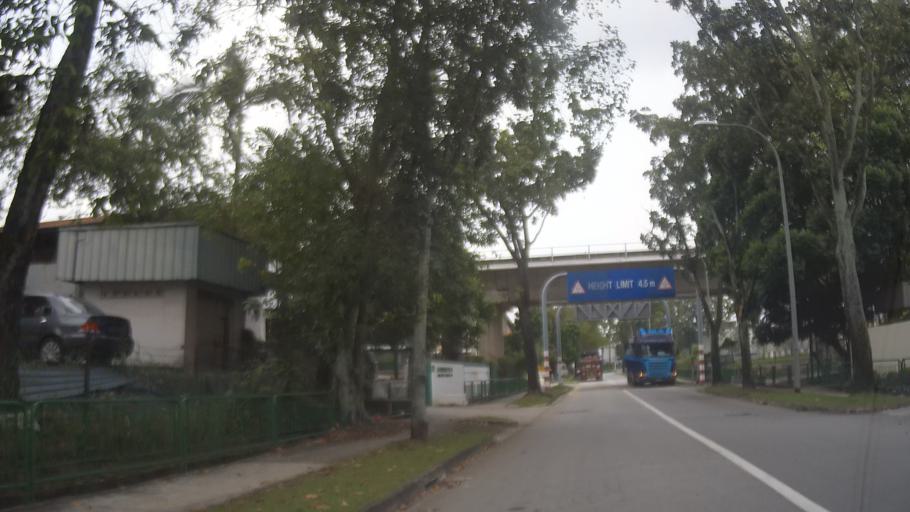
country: MY
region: Johor
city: Johor Bahru
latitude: 1.4098
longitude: 103.7501
